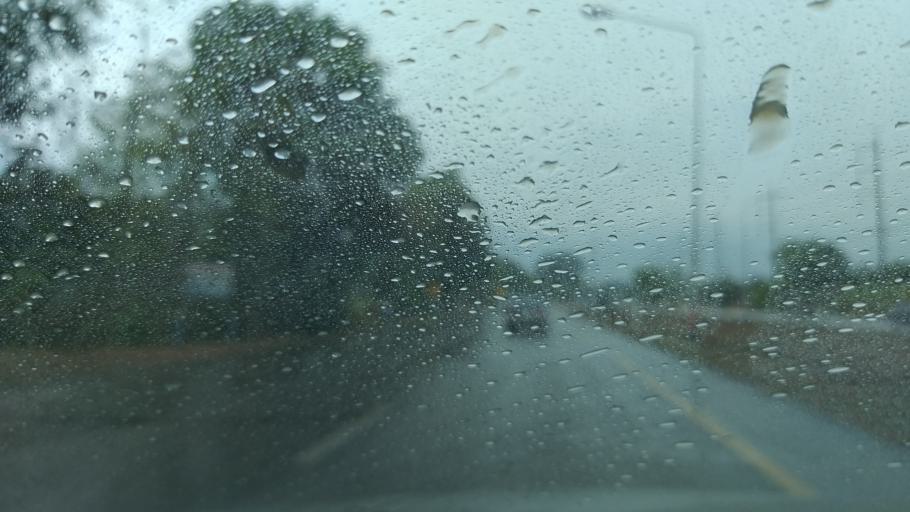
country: TH
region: Trat
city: Khao Saming
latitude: 12.3971
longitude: 102.3528
